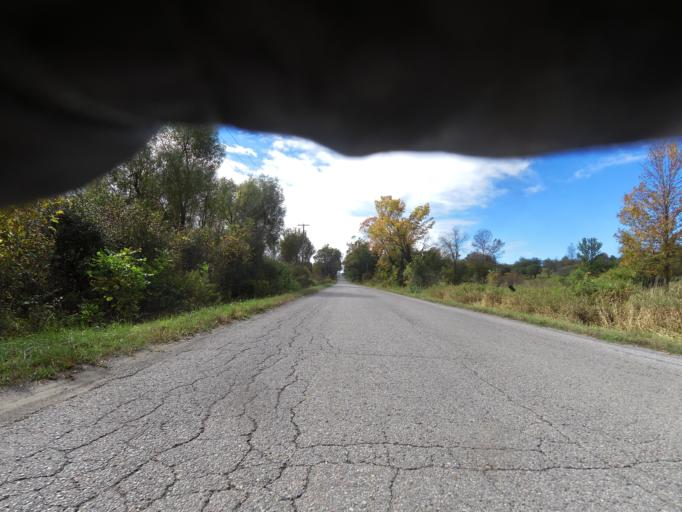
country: CA
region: Ontario
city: Cobourg
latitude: 43.9341
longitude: -78.3779
